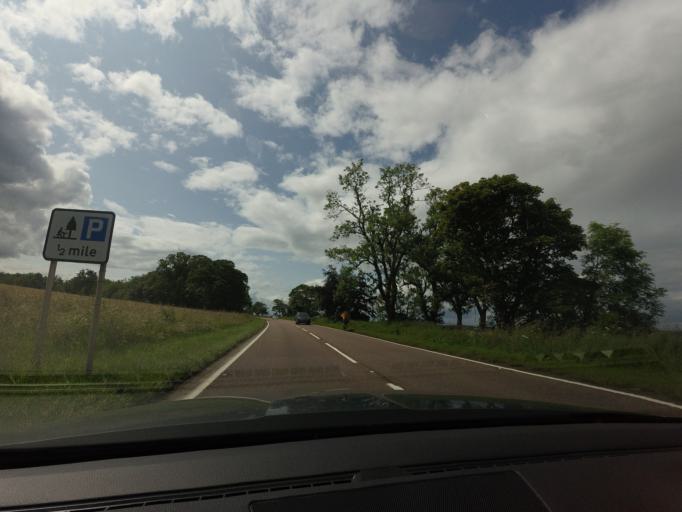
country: GB
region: Scotland
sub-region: Moray
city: Hopeman
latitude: 57.6489
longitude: -3.4240
